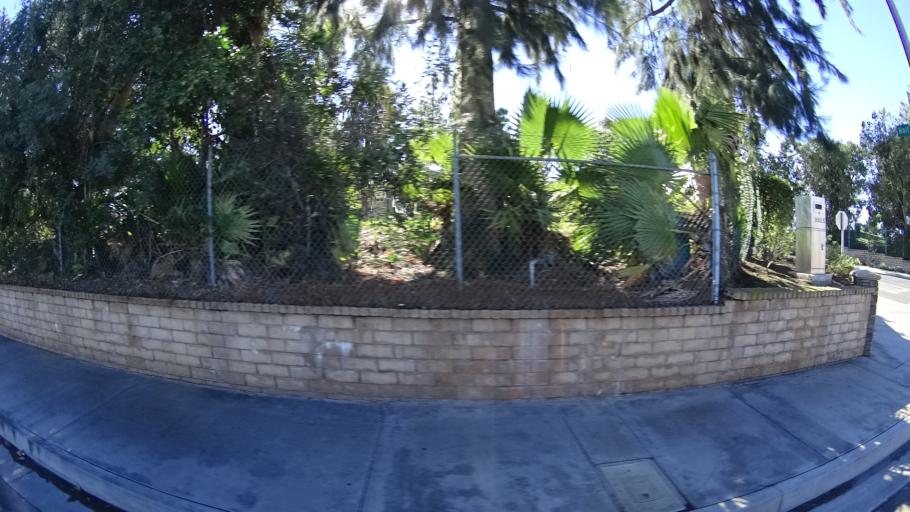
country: US
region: California
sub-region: Orange County
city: Placentia
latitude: 33.8841
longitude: -117.8498
